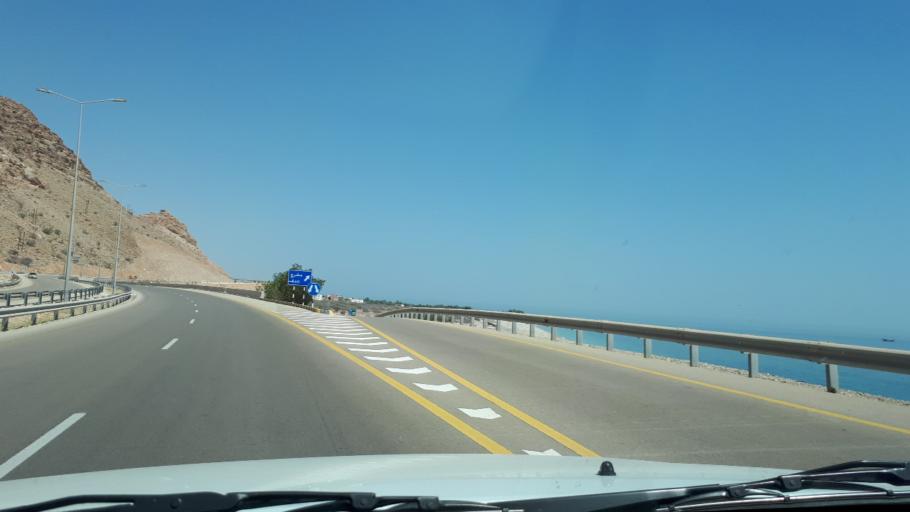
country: OM
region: Ash Sharqiyah
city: Sur
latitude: 22.8141
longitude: 59.2651
